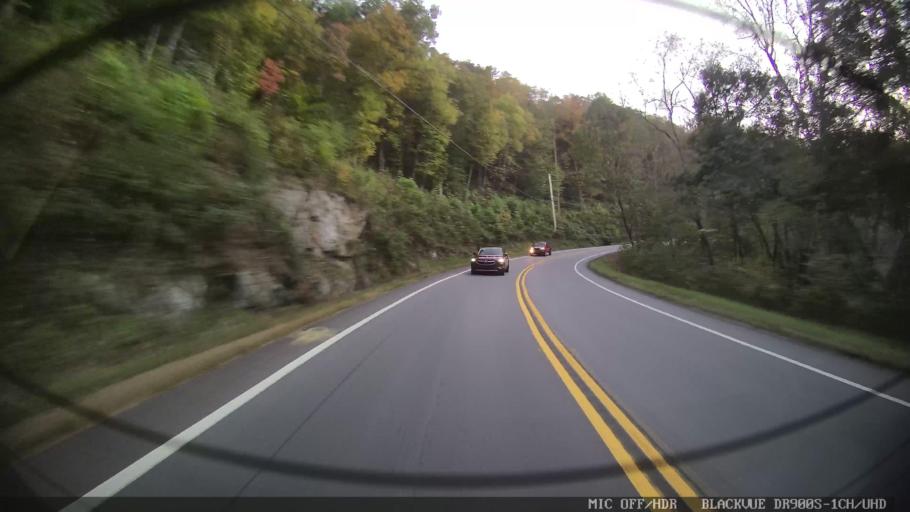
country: US
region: Georgia
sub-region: Union County
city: Blairsville
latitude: 34.7823
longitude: -83.9066
